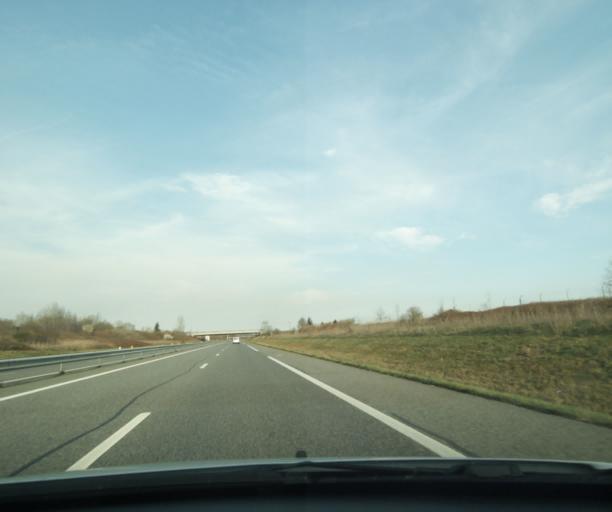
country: FR
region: Midi-Pyrenees
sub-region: Departement de la Haute-Garonne
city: Villeneuve-de-Riviere
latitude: 43.1125
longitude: 0.6309
